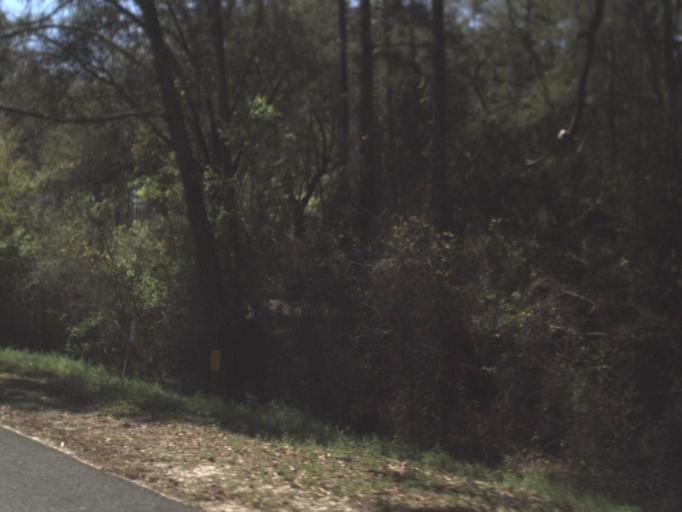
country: US
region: Florida
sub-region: Leon County
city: Woodville
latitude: 30.3544
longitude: -84.2608
